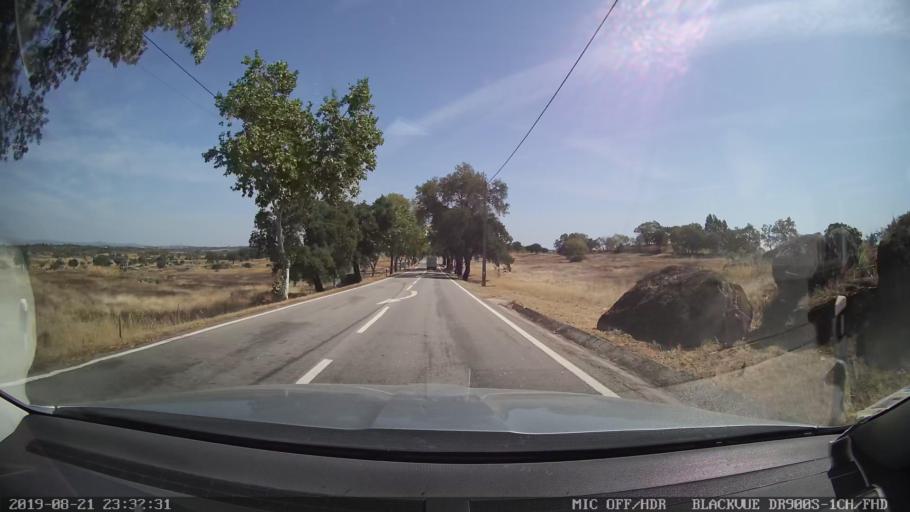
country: PT
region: Guarda
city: Alcains
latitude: 39.8792
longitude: -7.4119
